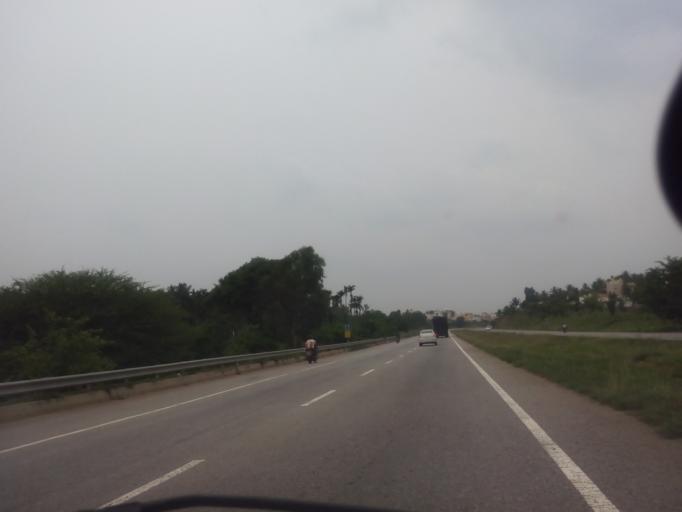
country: IN
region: Karnataka
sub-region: Bangalore Urban
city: Bangalore
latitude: 12.9791
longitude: 77.4709
